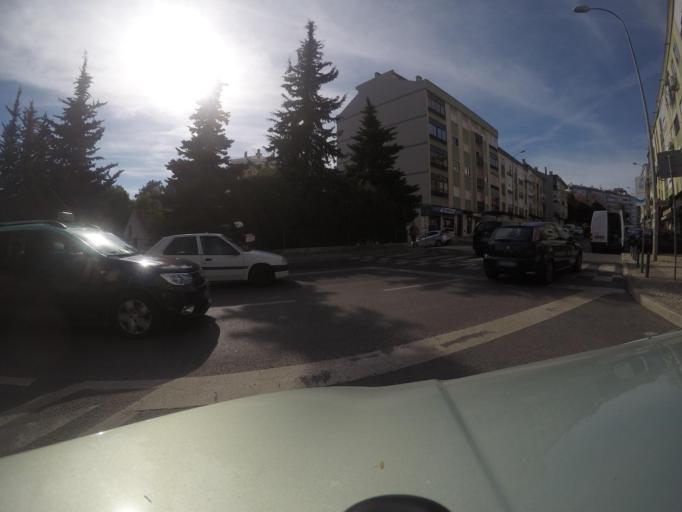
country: PT
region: Lisbon
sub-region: Amadora
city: Amadora
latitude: 38.7647
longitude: -9.2300
